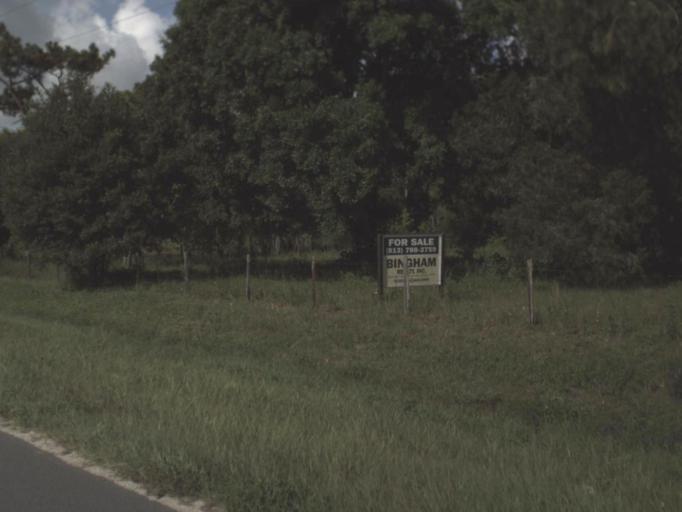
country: US
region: Florida
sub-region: Pasco County
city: Lacoochee
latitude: 28.4617
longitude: -82.1841
